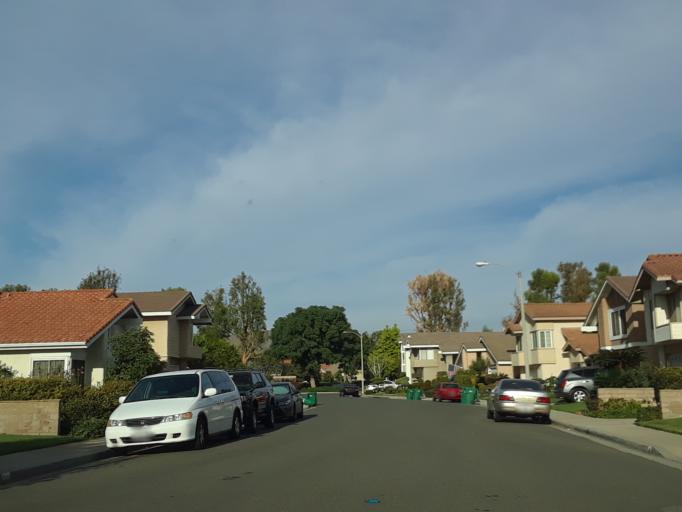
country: US
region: California
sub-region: Orange County
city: North Tustin
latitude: 33.7183
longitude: -117.7623
